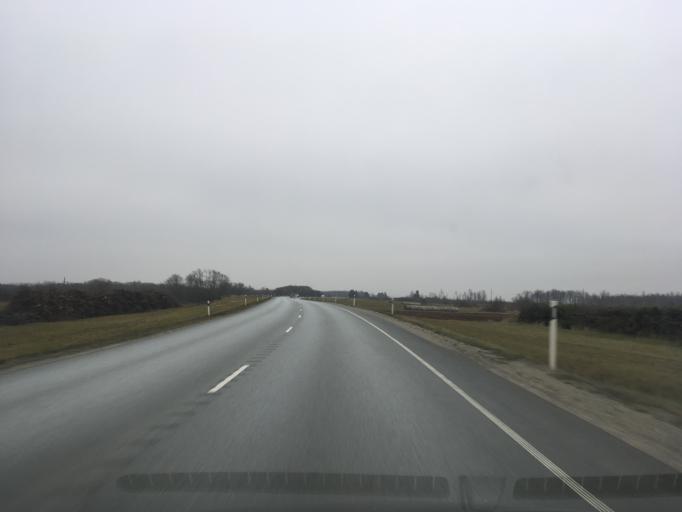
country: EE
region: Ida-Virumaa
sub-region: Kivioli linn
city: Kivioli
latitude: 59.4270
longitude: 26.9574
